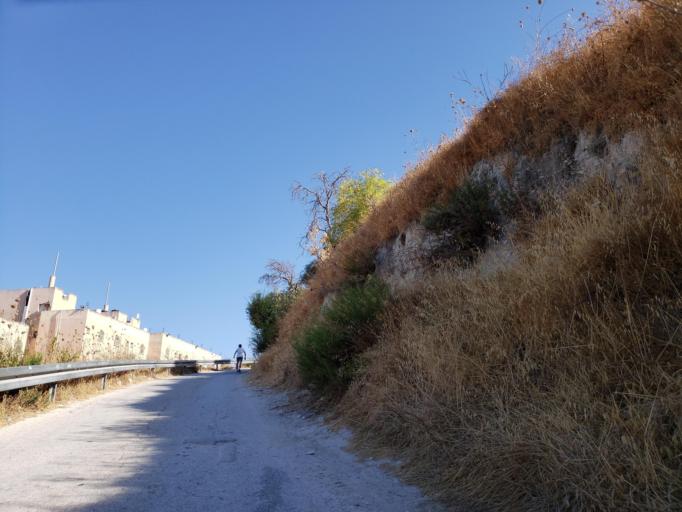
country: IL
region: Northern District
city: Safed
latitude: 32.9660
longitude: 35.4905
